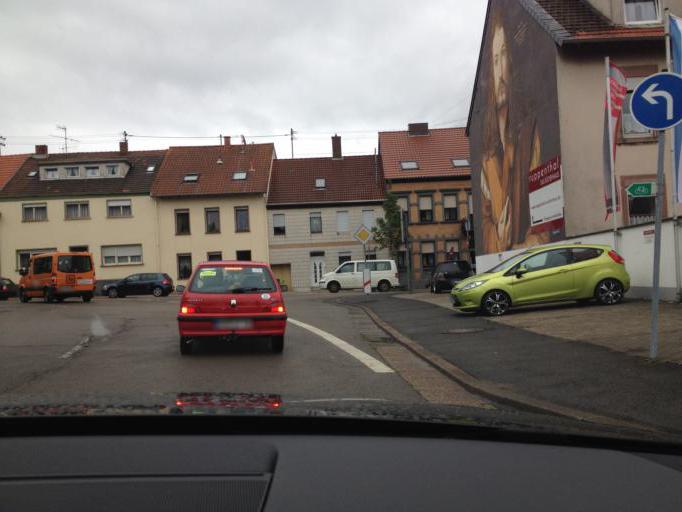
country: DE
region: Saarland
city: Sankt Wendel
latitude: 49.4704
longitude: 7.1678
